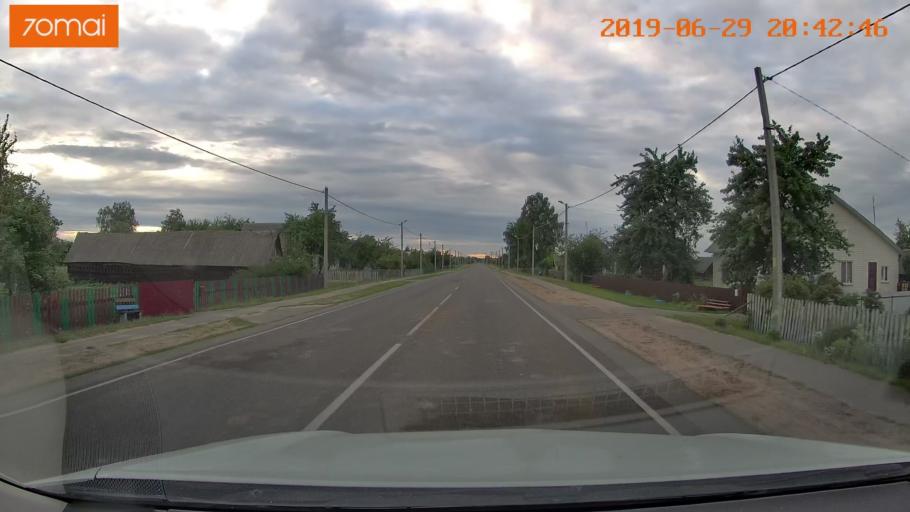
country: BY
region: Brest
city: Hantsavichy
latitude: 52.6001
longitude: 26.3225
